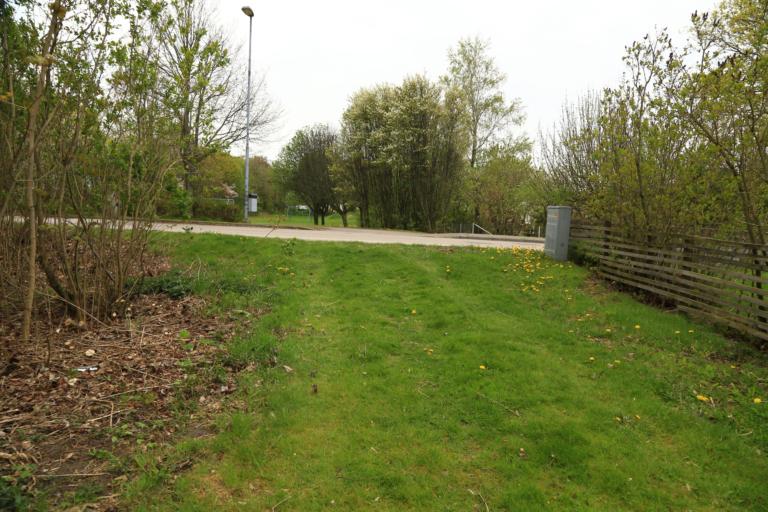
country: SE
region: Halland
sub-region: Varbergs Kommun
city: Varberg
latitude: 57.1260
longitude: 12.2762
